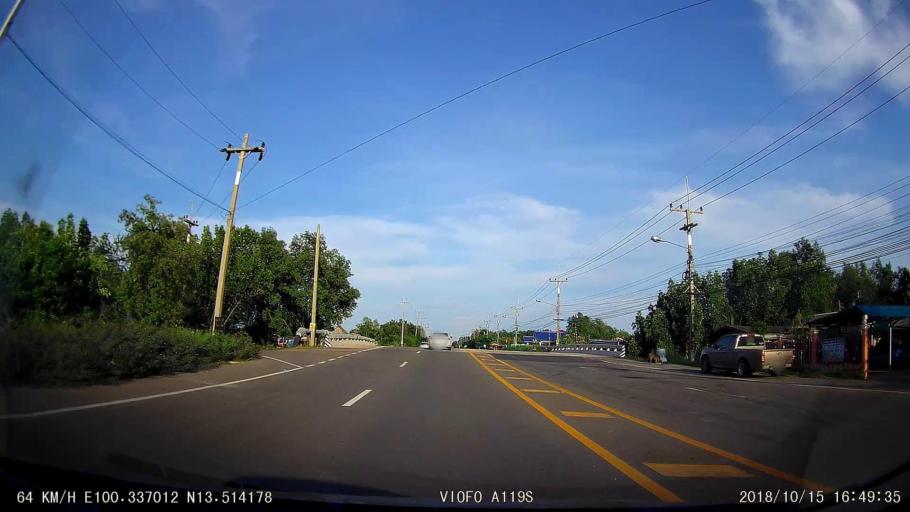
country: TH
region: Samut Sakhon
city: Samut Sakhon
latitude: 13.5142
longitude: 100.3370
